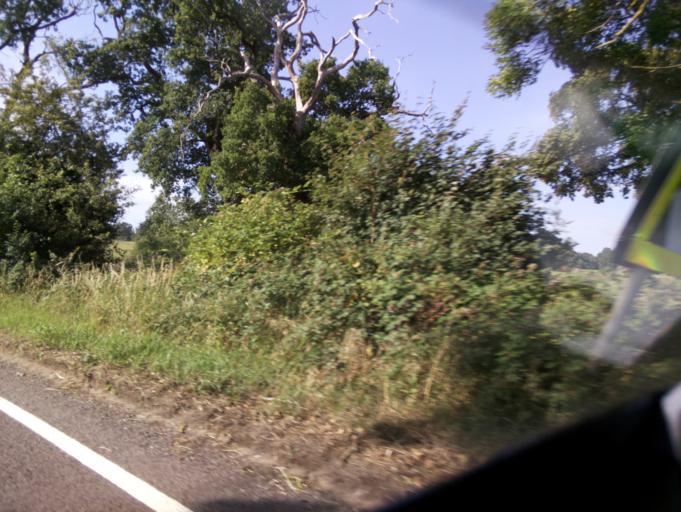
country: GB
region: England
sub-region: Oxfordshire
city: Faringdon
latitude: 51.6655
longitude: -1.5861
